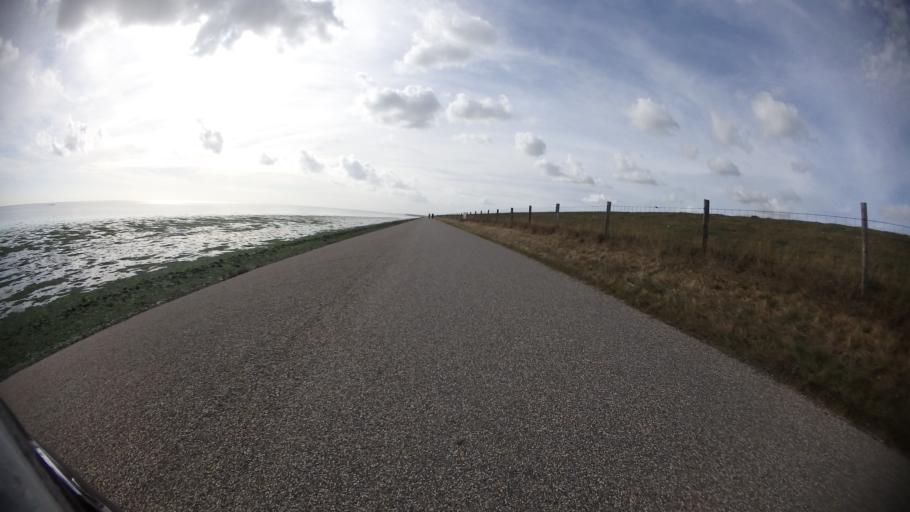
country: NL
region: North Holland
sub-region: Gemeente Texel
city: Den Burg
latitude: 53.1130
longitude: 4.8988
